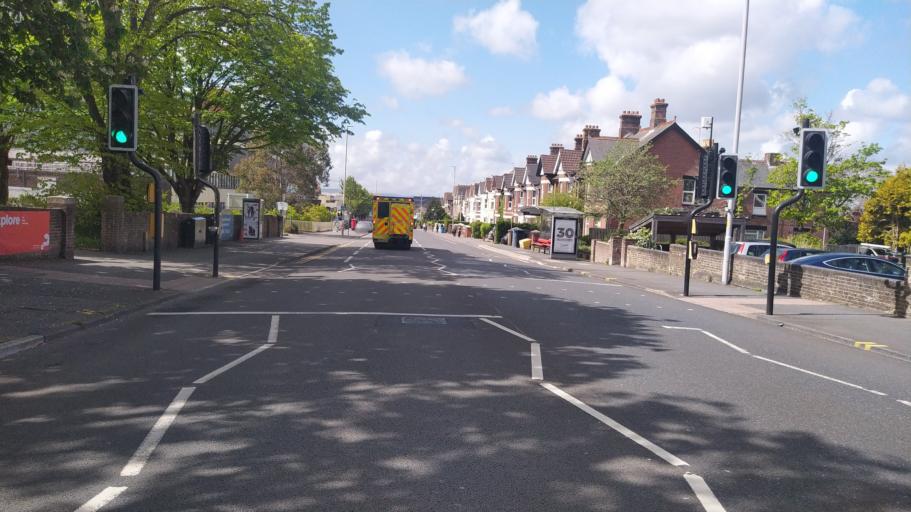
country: GB
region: England
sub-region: Dorset
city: Parkstone
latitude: 50.7230
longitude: -1.9718
